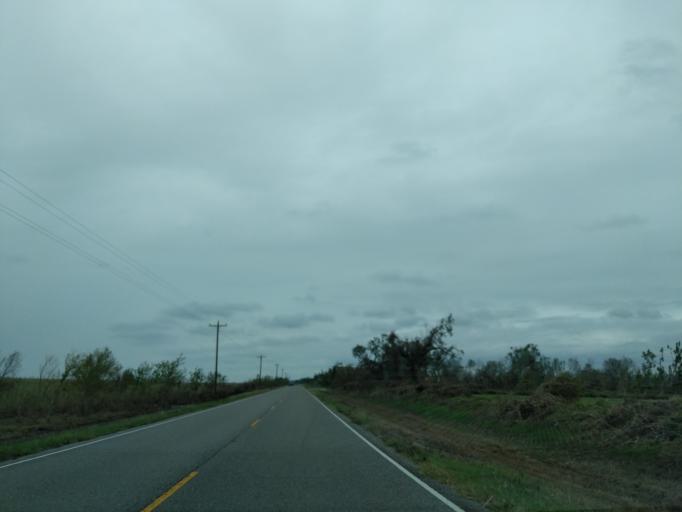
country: US
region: Louisiana
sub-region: Cameron Parish
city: Cameron
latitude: 29.7869
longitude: -93.1467
